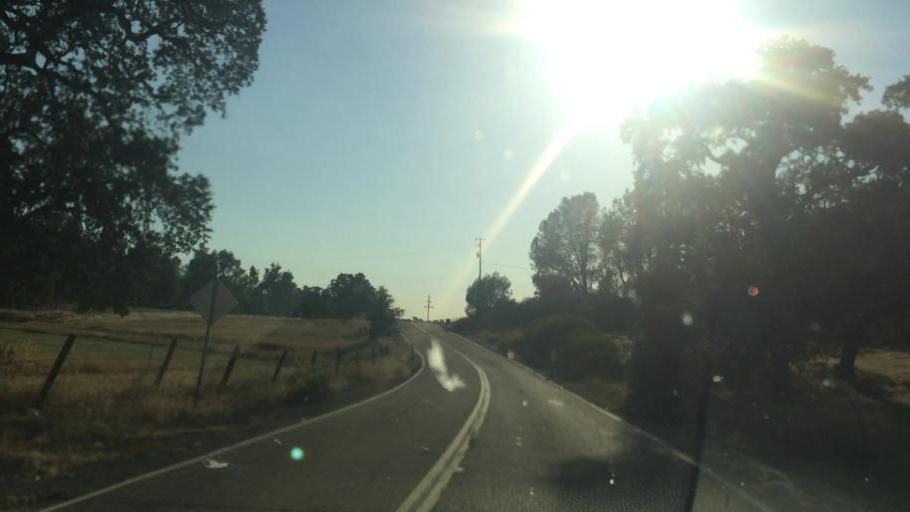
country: US
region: California
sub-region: Amador County
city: Plymouth
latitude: 38.4858
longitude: -120.9082
